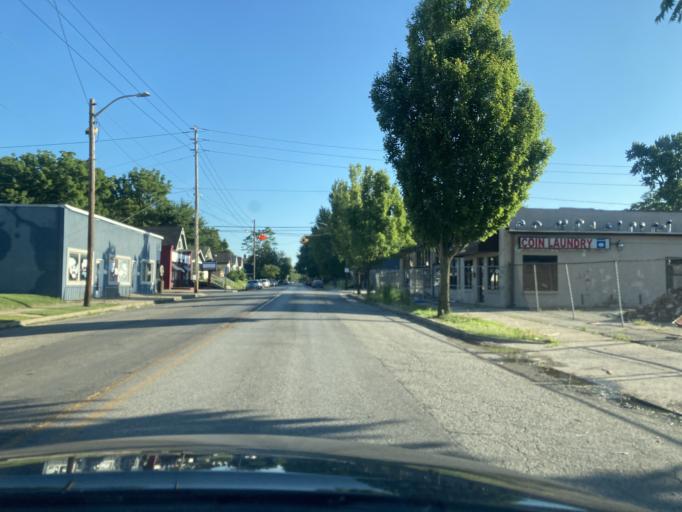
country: US
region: Indiana
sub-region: Marion County
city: Broad Ripple
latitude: 39.8277
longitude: -86.1640
